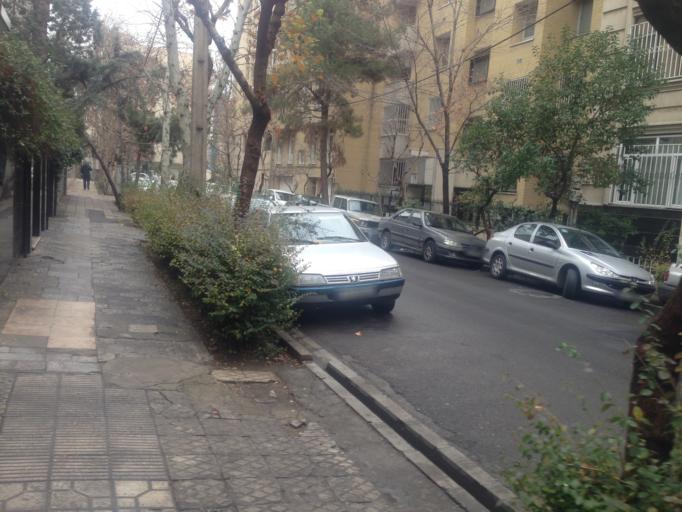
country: IR
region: Tehran
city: Tehran
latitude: 35.7376
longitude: 51.4069
